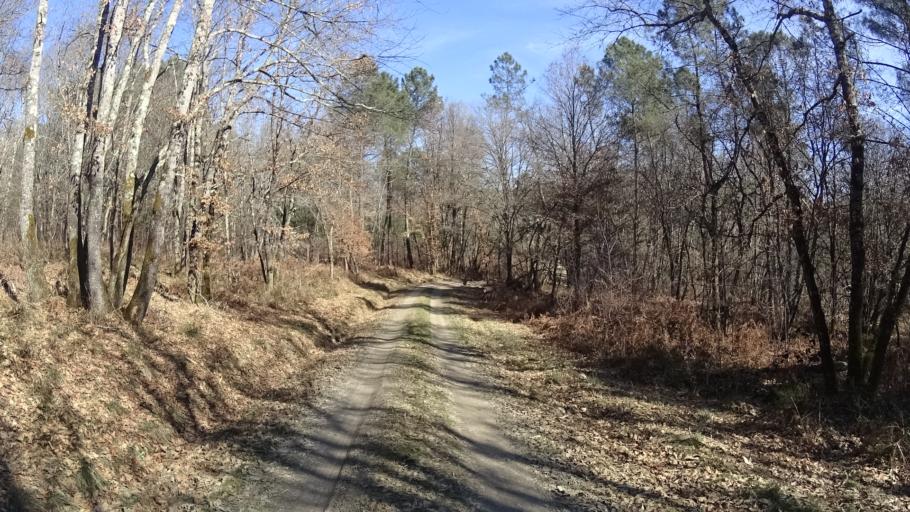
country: FR
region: Aquitaine
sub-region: Departement de la Dordogne
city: Riberac
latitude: 45.1868
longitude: 0.2977
